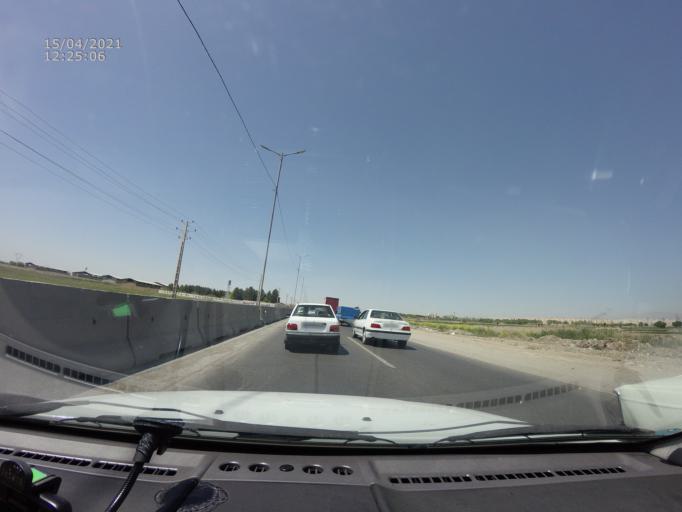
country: IR
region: Tehran
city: Eslamshahr
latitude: 35.5121
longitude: 51.2496
